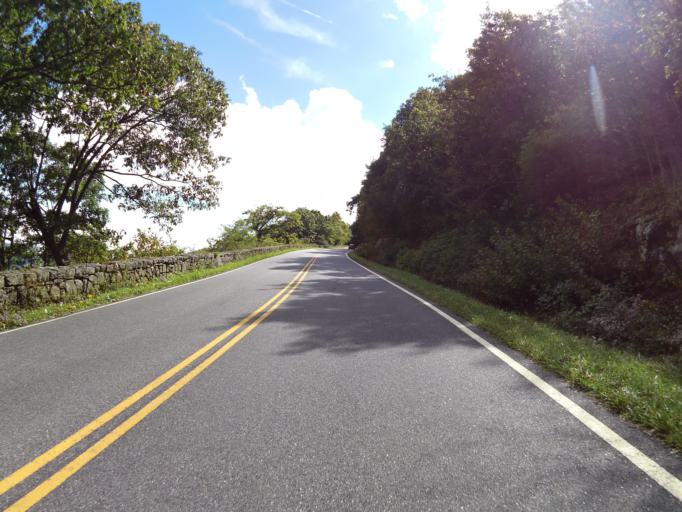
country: US
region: Virginia
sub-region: Page County
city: Luray
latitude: 38.5913
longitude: -78.3603
